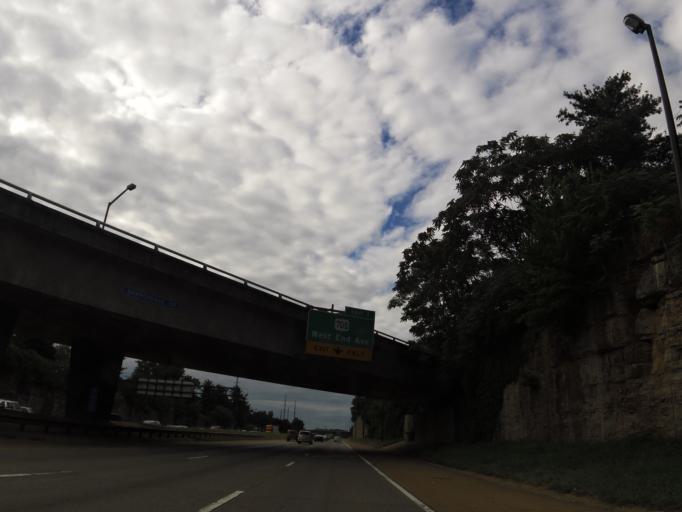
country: US
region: Tennessee
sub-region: Davidson County
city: Nashville
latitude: 36.1294
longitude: -86.8163
